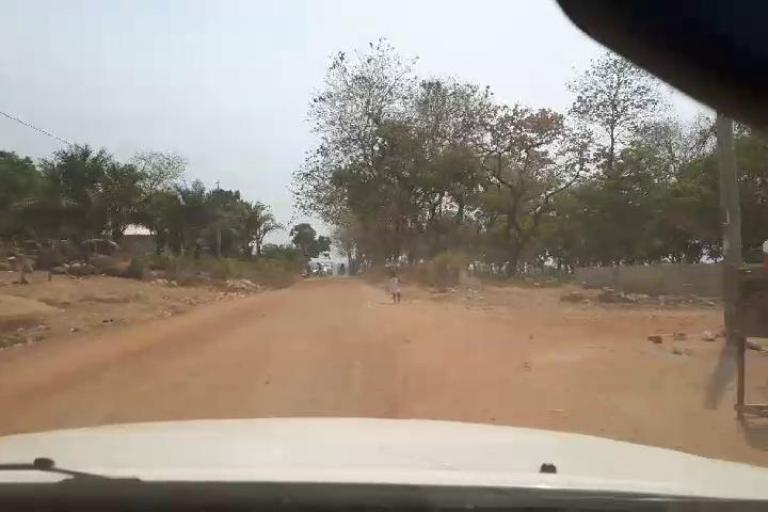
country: SL
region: Northern Province
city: Bumbuna
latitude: 9.0381
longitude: -11.7586
